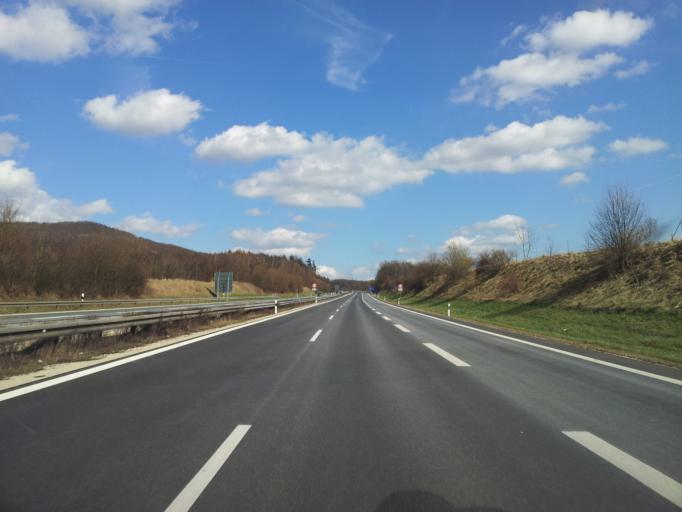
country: DE
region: Bavaria
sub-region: Upper Franconia
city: Schesslitz
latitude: 49.9825
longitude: 11.0466
